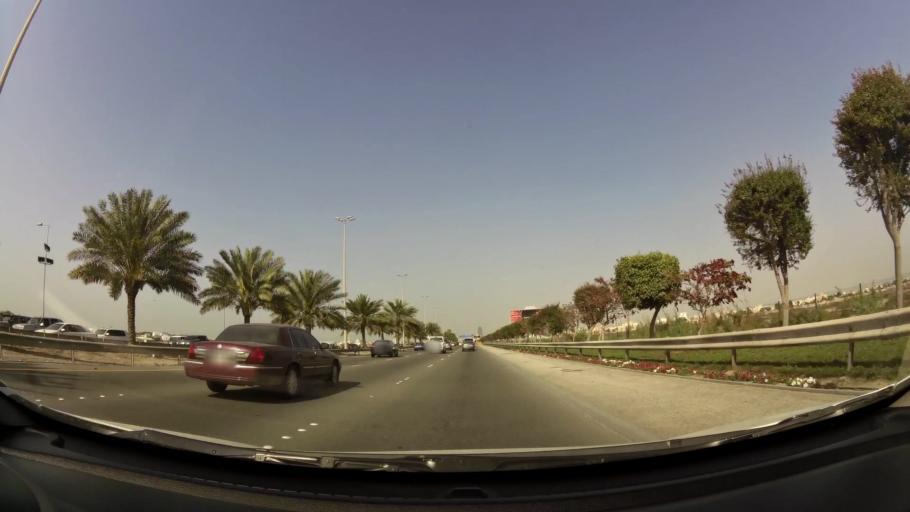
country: BH
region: Manama
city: Jidd Hafs
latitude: 26.2017
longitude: 50.5120
